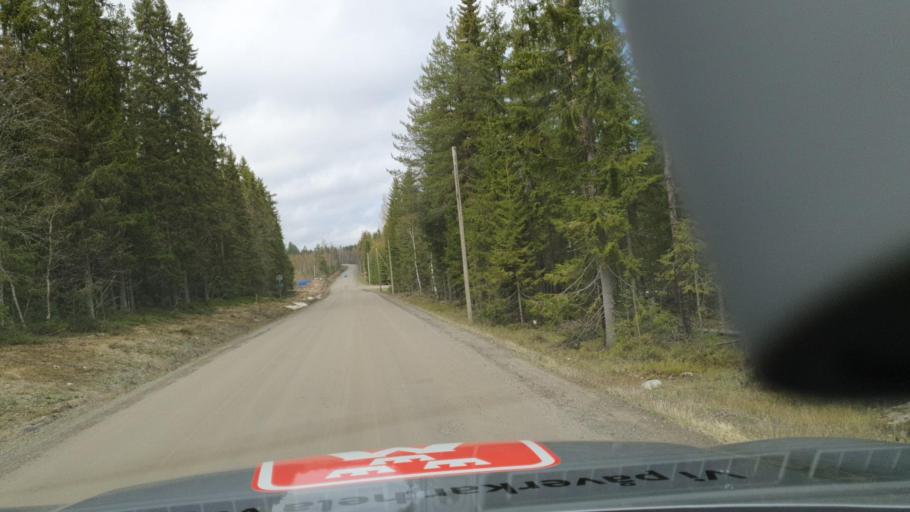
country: SE
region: Vaesterbotten
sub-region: Bjurholms Kommun
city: Bjurholm
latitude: 63.6778
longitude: 18.9900
